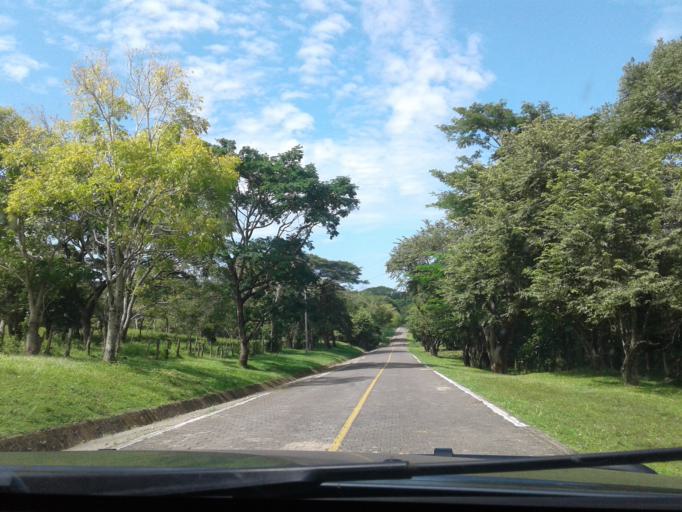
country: NI
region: Rivas
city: Cardenas
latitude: 11.1752
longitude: -85.4853
